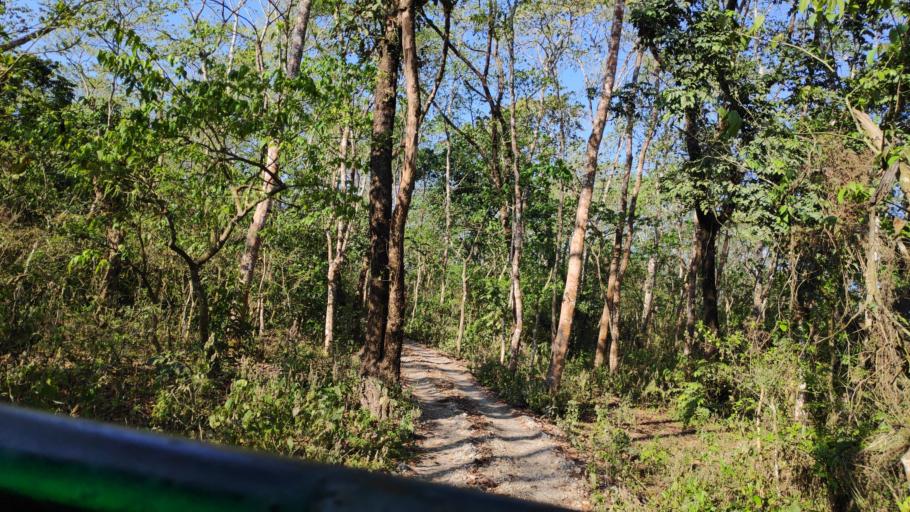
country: NP
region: Central Region
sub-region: Narayani Zone
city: Bharatpur
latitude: 27.5617
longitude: 84.5328
